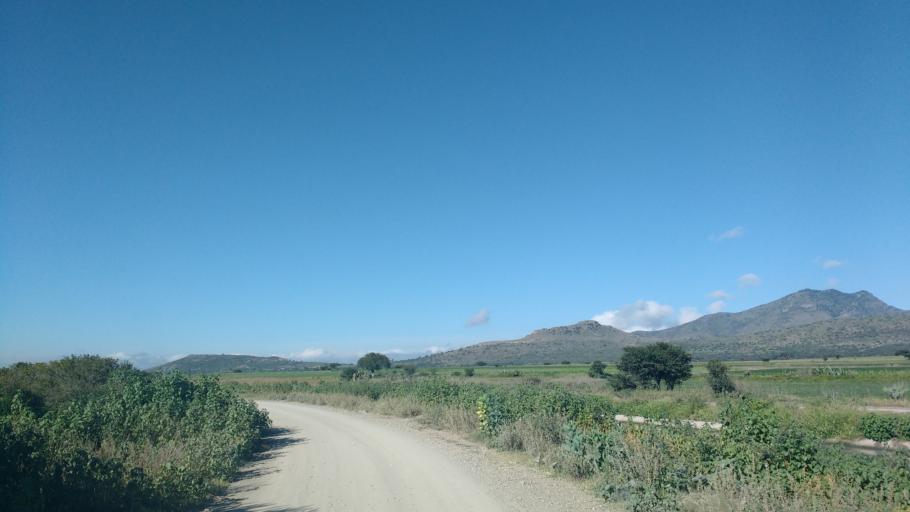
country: MX
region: Hidalgo
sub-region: Tezontepec de Aldama
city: Tenango
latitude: 20.2531
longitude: -99.2541
